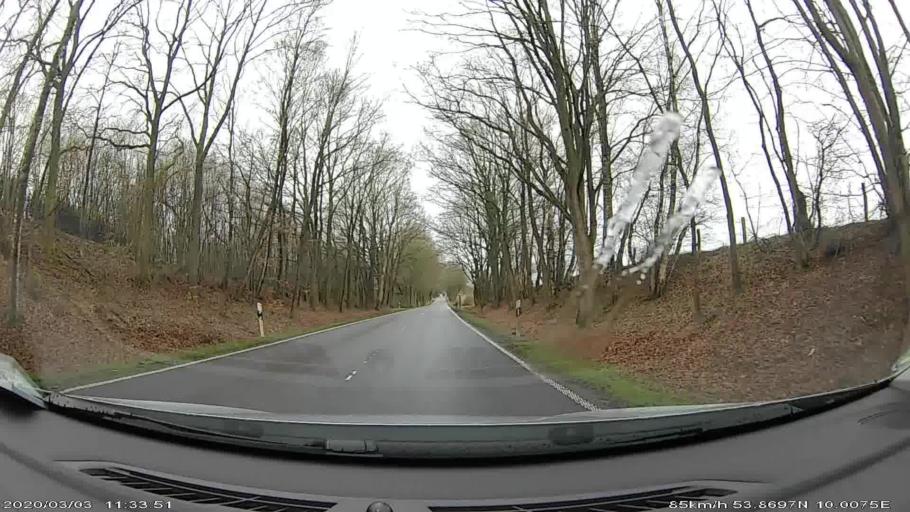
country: DE
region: Schleswig-Holstein
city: Kattendorf
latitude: 53.8714
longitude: 10.0023
